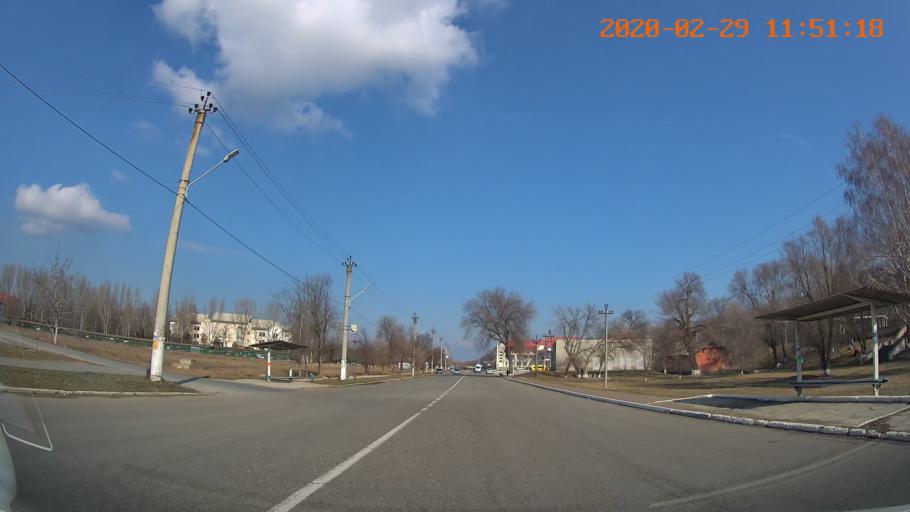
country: MD
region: Telenesti
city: Ribnita
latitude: 47.7643
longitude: 28.9899
